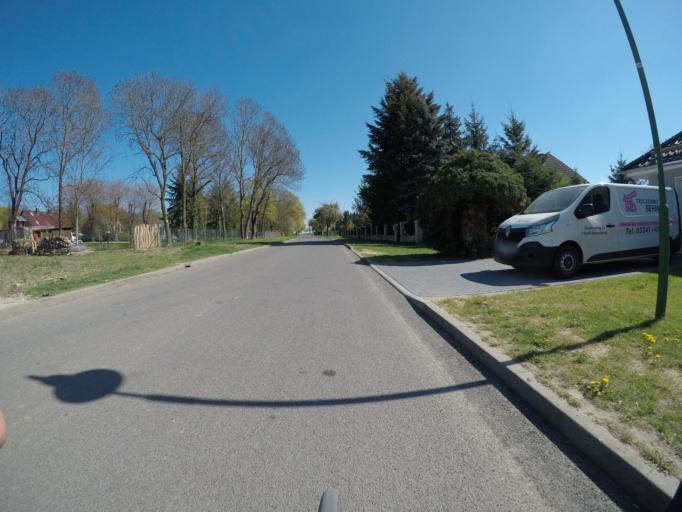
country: DE
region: Brandenburg
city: Werftpfuhl
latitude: 52.6358
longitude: 13.8012
